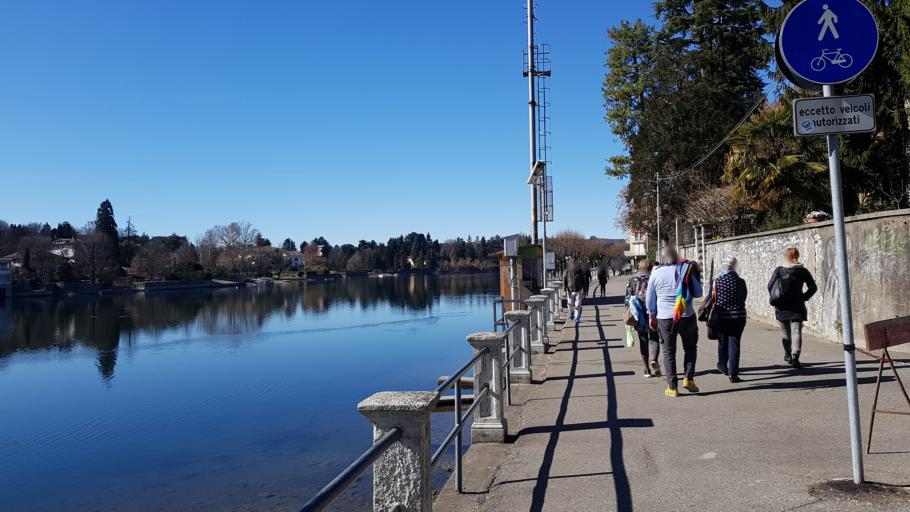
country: IT
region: Lombardy
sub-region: Provincia di Varese
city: Sesto Calende
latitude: 45.7244
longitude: 8.6381
